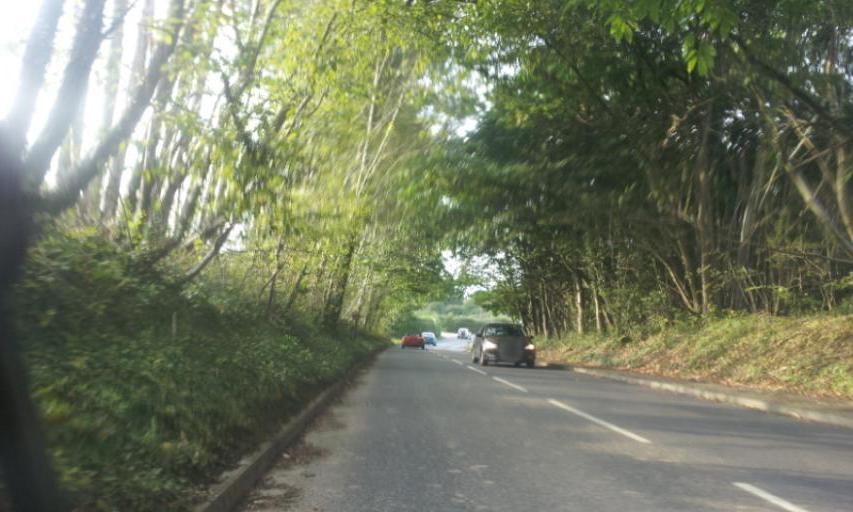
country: GB
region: England
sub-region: Kent
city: Wateringbury
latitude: 51.2657
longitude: 0.4304
